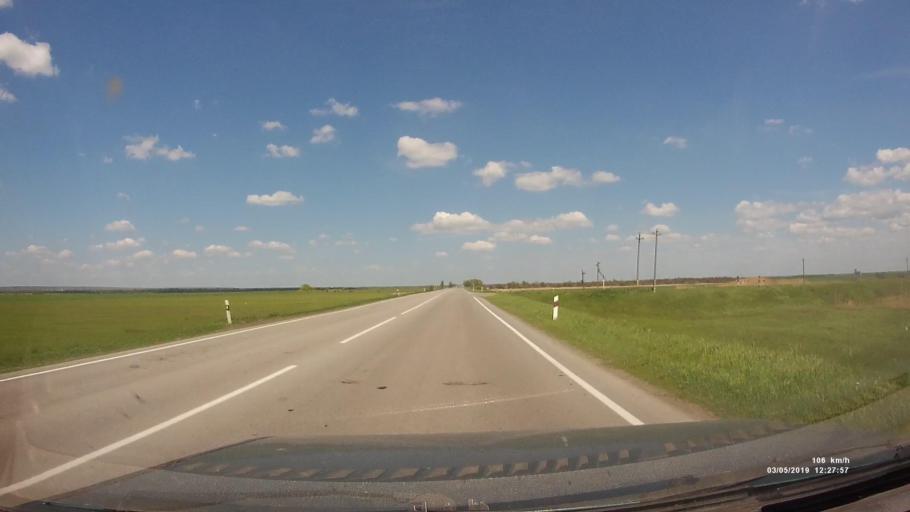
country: RU
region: Rostov
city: Semikarakorsk
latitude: 47.4661
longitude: 40.7245
